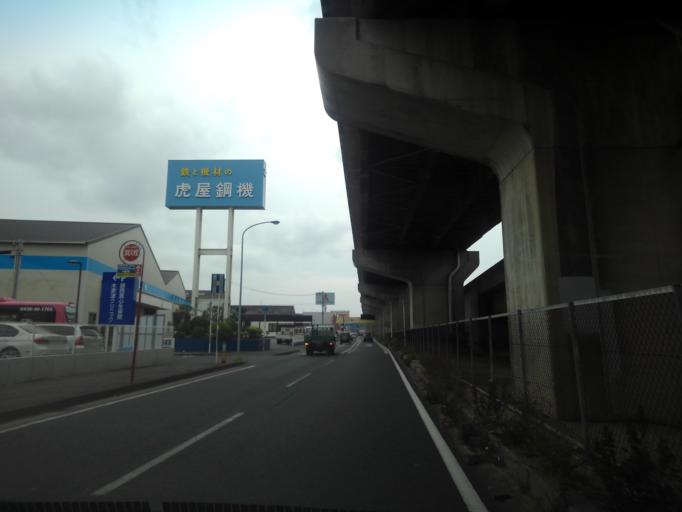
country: JP
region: Chiba
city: Kisarazu
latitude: 35.3714
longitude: 139.9315
